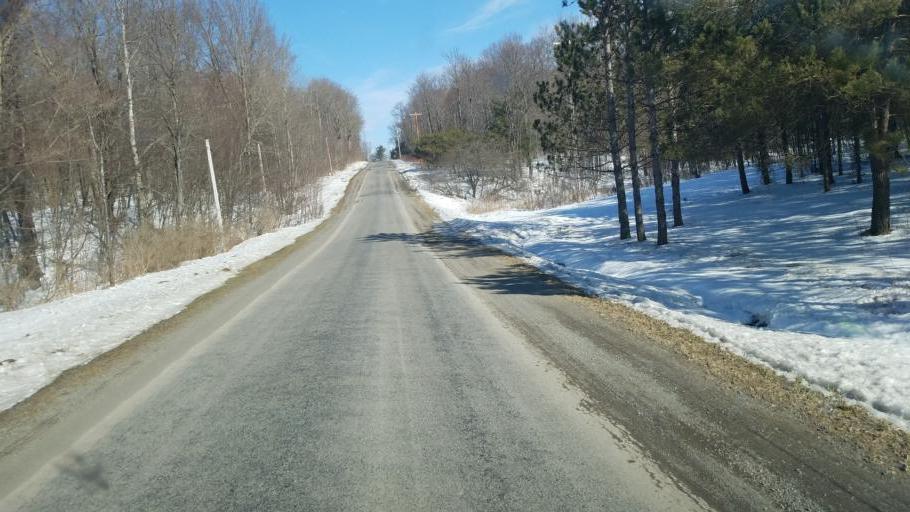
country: US
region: New York
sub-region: Allegany County
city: Andover
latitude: 42.0835
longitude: -77.7716
